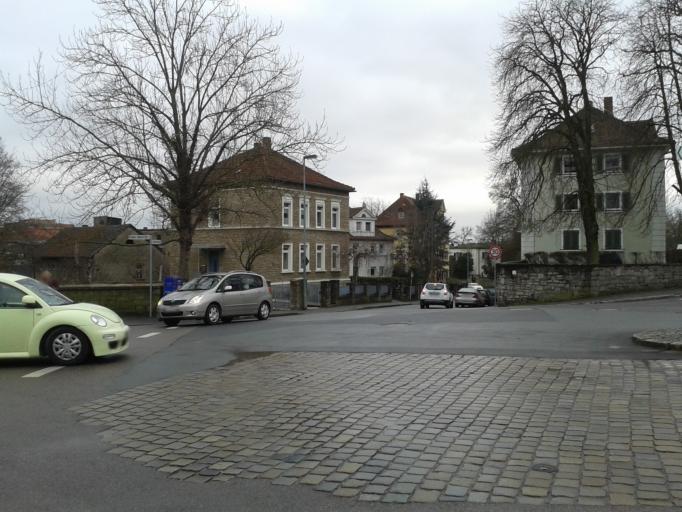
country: DE
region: Bavaria
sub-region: Regierungsbezirk Unterfranken
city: Kitzingen
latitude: 49.7327
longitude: 10.1560
